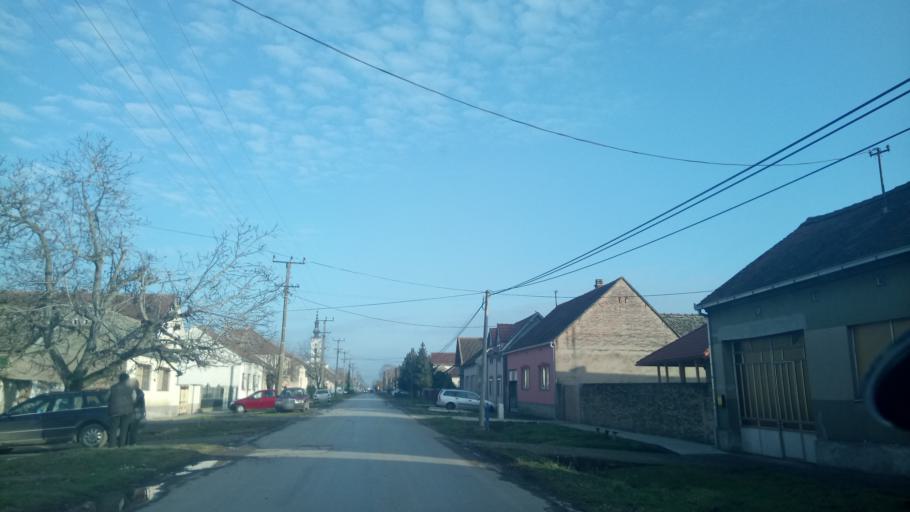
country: RS
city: Vojka
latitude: 44.9359
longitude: 20.1467
